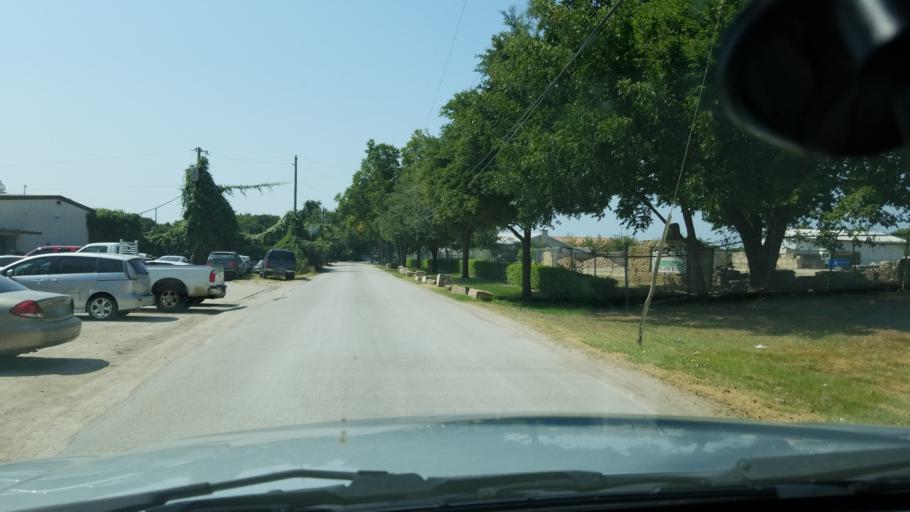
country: US
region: Texas
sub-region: Dallas County
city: Irving
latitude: 32.8623
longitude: -96.9059
